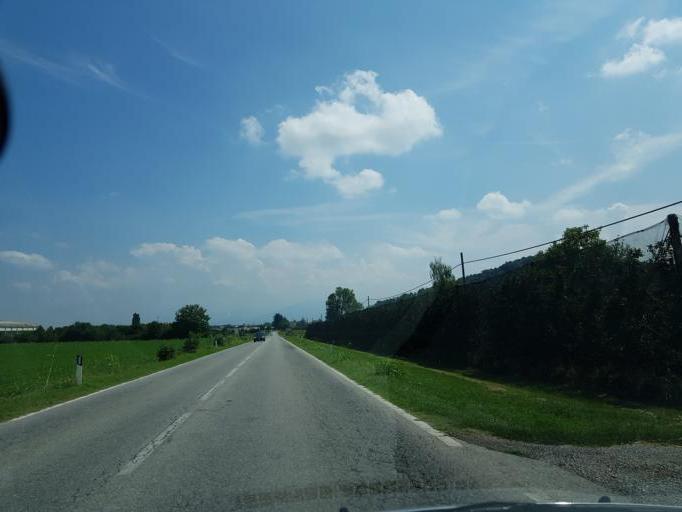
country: IT
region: Piedmont
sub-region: Provincia di Cuneo
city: Caraglio
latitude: 44.4370
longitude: 7.4162
